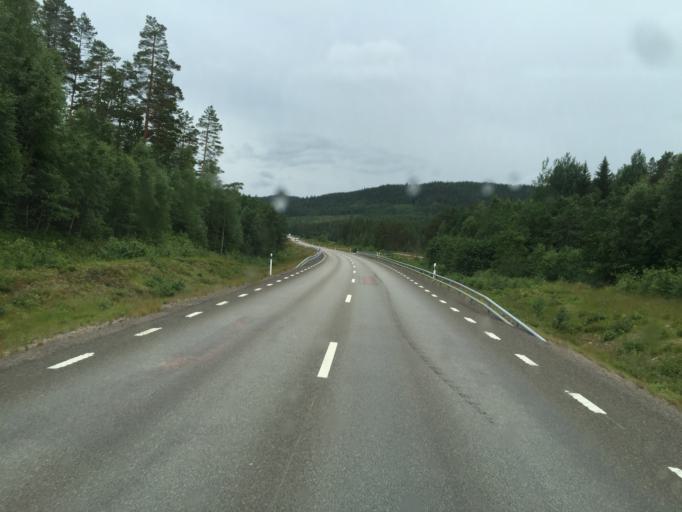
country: SE
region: Dalarna
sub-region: Malung-Saelens kommun
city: Malung
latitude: 60.6454
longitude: 13.6284
